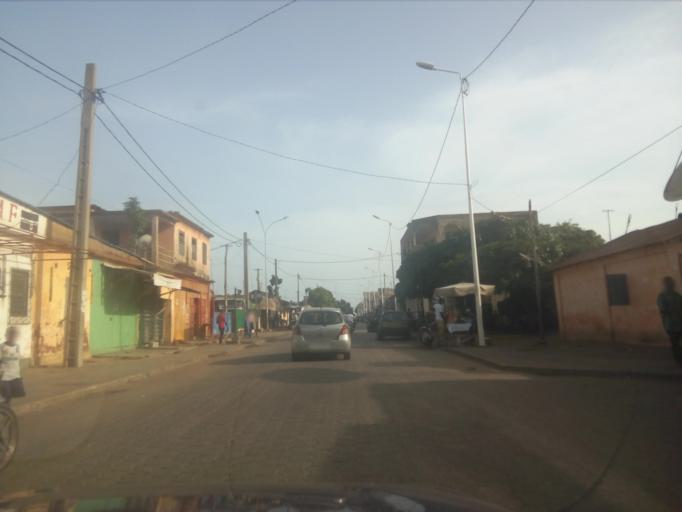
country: TG
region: Maritime
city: Lome
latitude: 6.1426
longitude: 1.2285
